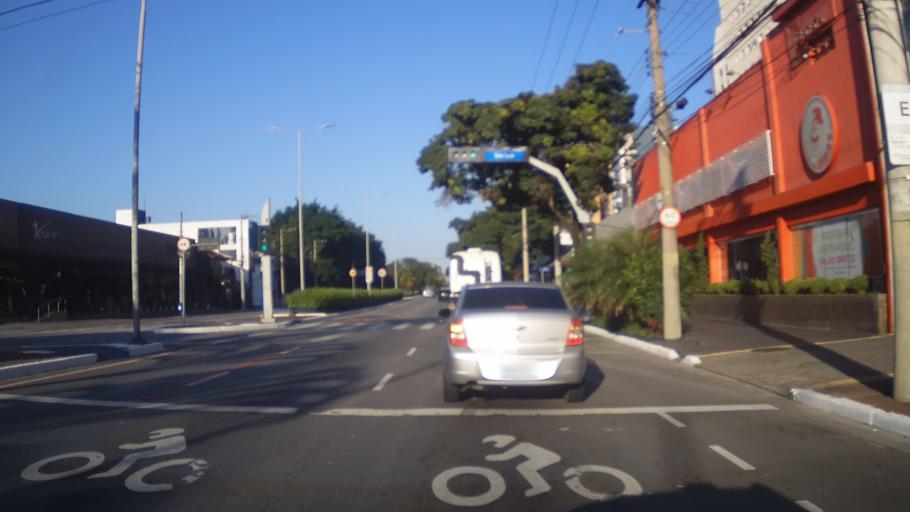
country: BR
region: Sao Paulo
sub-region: Sao Caetano Do Sul
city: Sao Caetano do Sul
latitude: -23.6165
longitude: -46.5657
